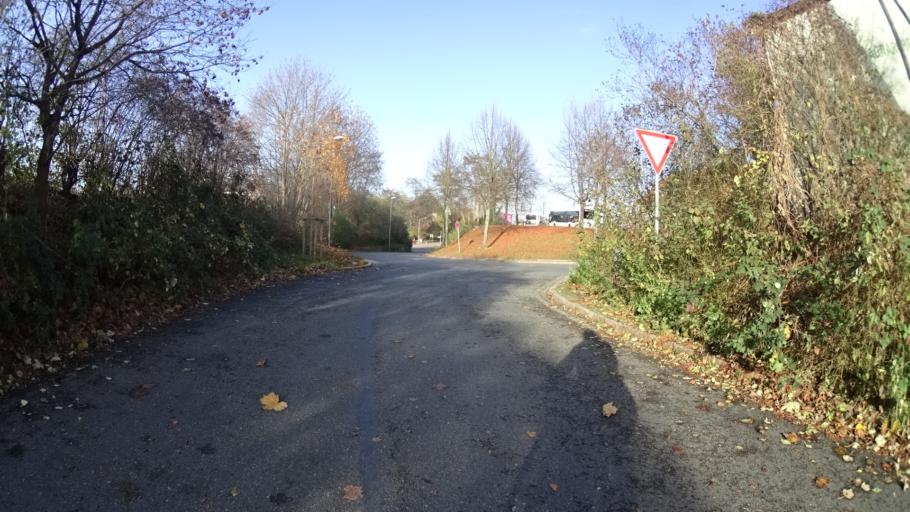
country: DE
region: Lower Saxony
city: Lueneburg
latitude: 53.2471
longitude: 10.4185
